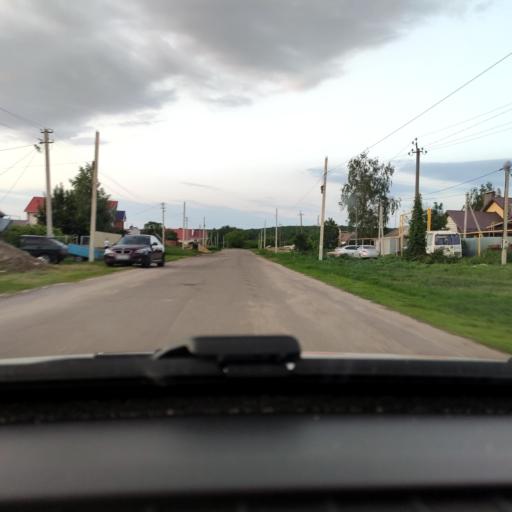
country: RU
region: Voronezj
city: Semiluki
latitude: 51.7482
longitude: 39.0236
